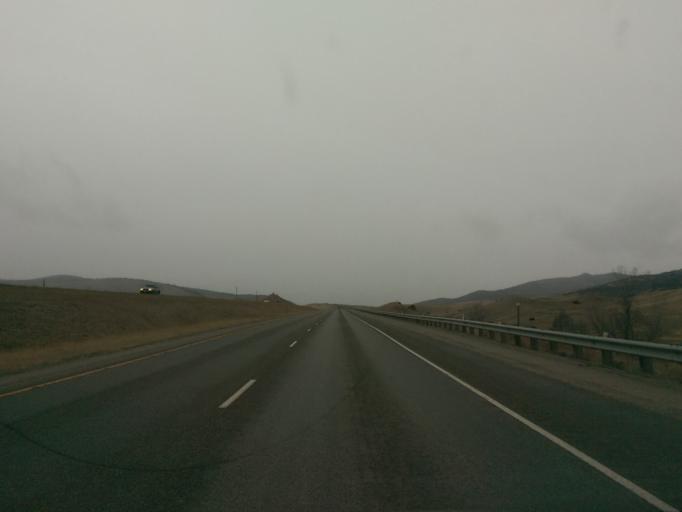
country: US
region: Montana
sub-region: Gallatin County
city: Three Forks
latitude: 45.9041
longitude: -111.8067
